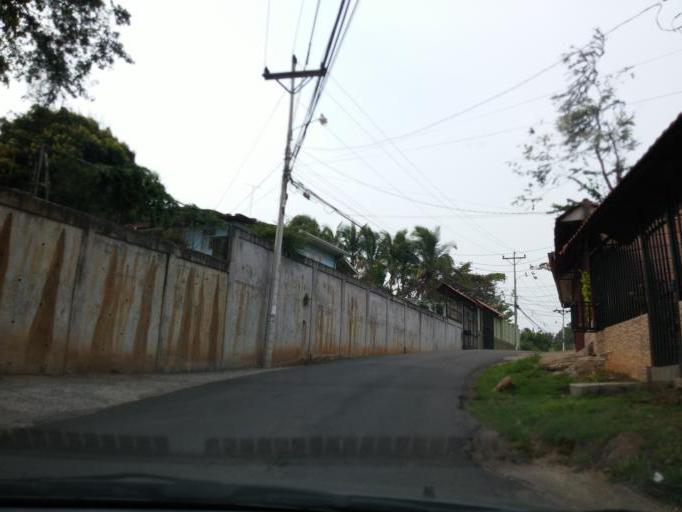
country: CR
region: Alajuela
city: Alajuela
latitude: 9.9918
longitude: -84.2305
